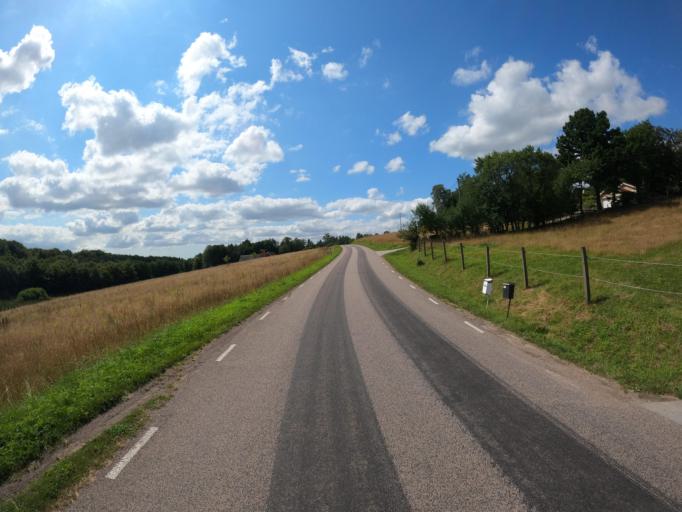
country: SE
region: Skane
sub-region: Lunds Kommun
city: Veberod
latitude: 55.5865
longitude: 13.4883
